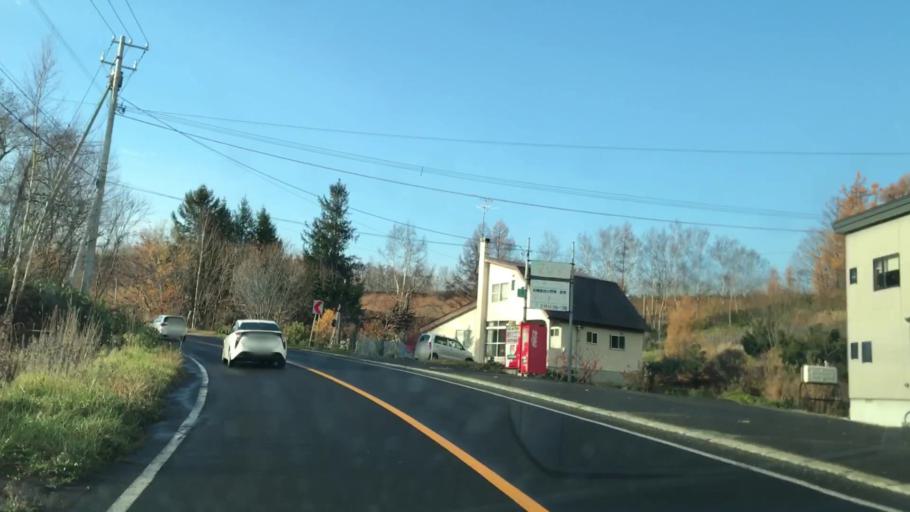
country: JP
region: Hokkaido
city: Yoichi
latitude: 43.1907
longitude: 140.8368
